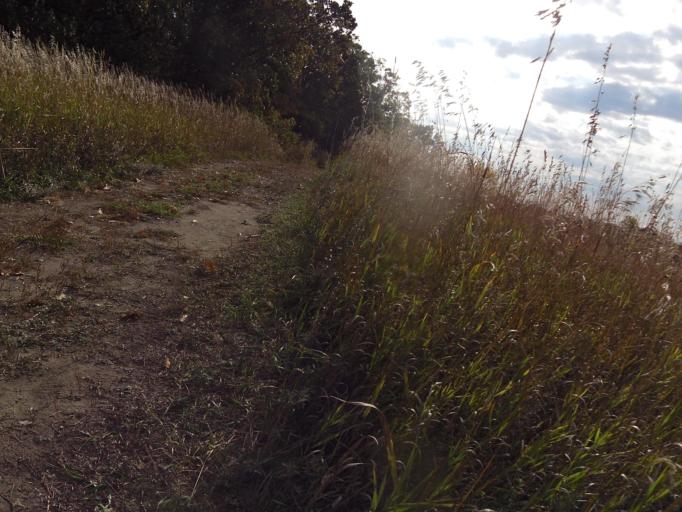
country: US
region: North Dakota
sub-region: Pembina County
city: Cavalier
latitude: 48.7808
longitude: -97.7457
